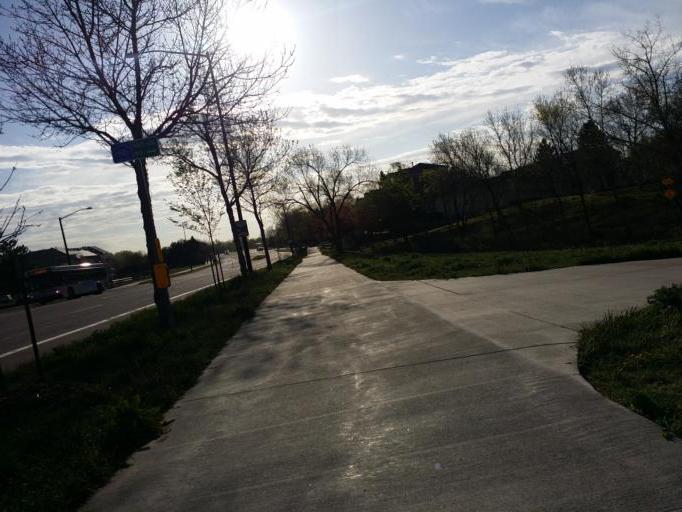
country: US
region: Colorado
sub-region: Boulder County
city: Boulder
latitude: 40.0073
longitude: -105.2467
